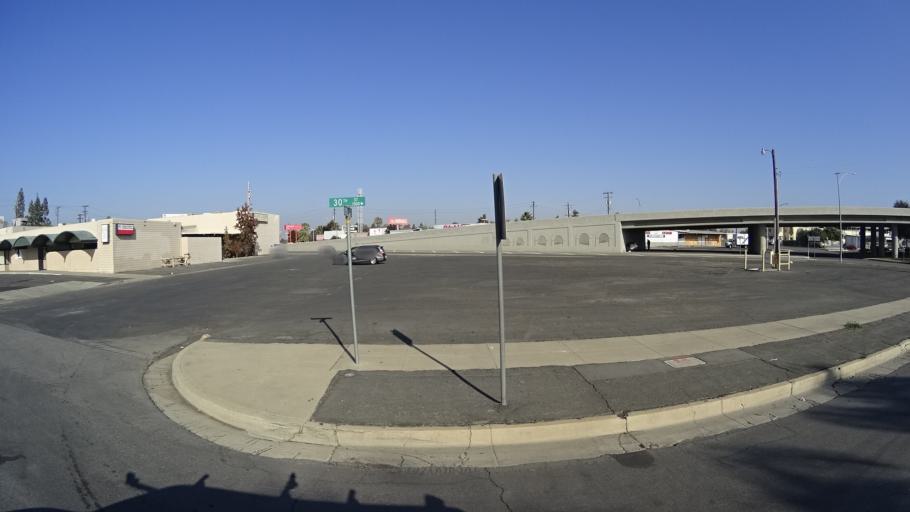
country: US
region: California
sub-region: Kern County
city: Bakersfield
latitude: 35.3867
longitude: -119.0199
